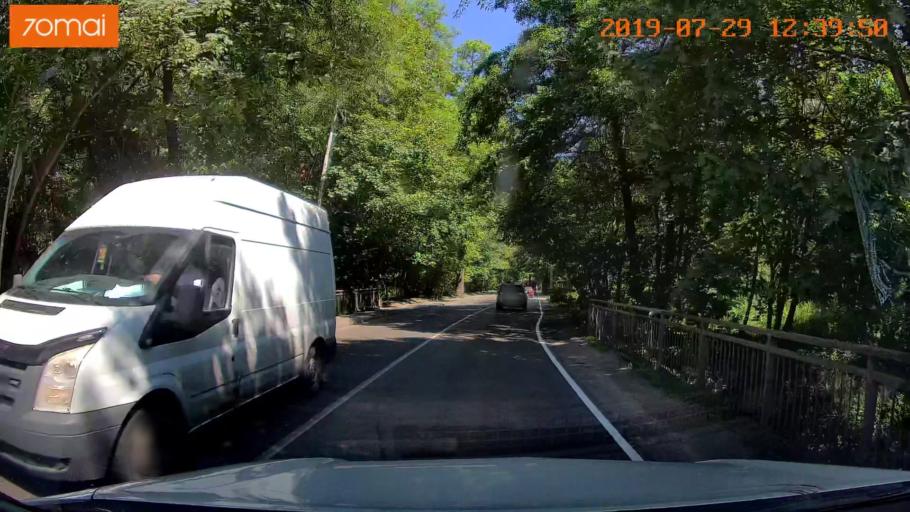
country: RU
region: Kaliningrad
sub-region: Gorod Kaliningrad
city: Kaliningrad
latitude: 54.6643
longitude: 20.5408
